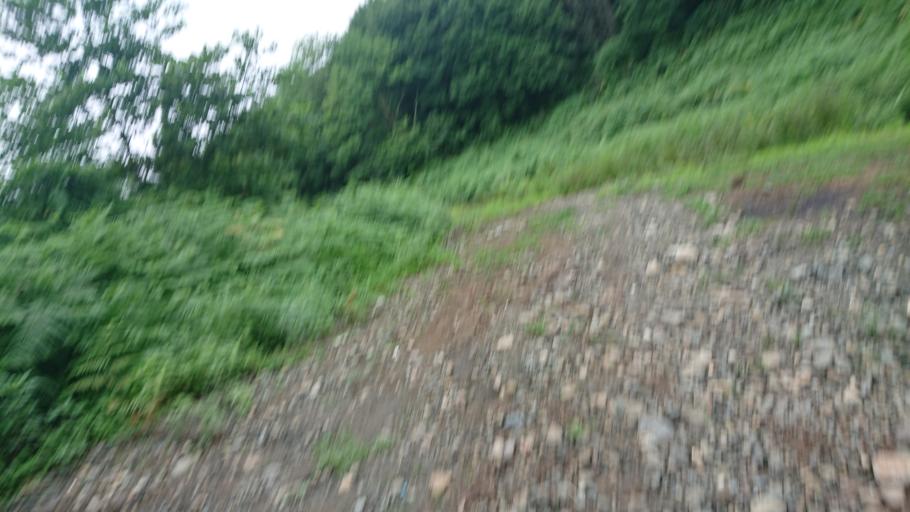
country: TR
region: Rize
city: Rize
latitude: 40.9876
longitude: 40.5060
